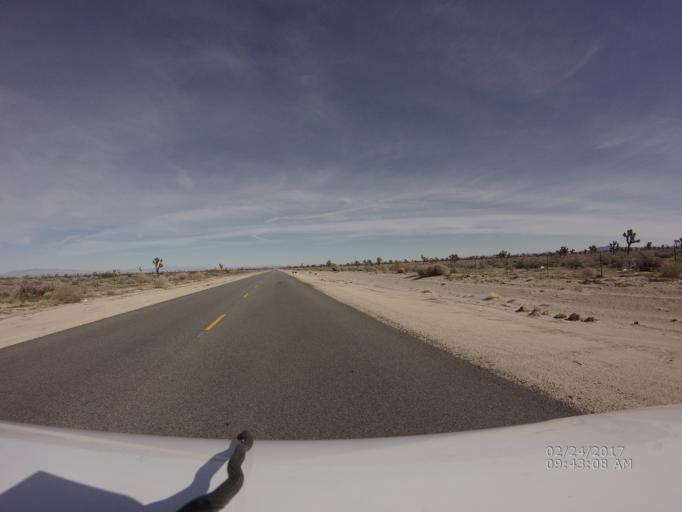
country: US
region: California
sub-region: Los Angeles County
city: Littlerock
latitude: 34.5835
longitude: -118.0050
